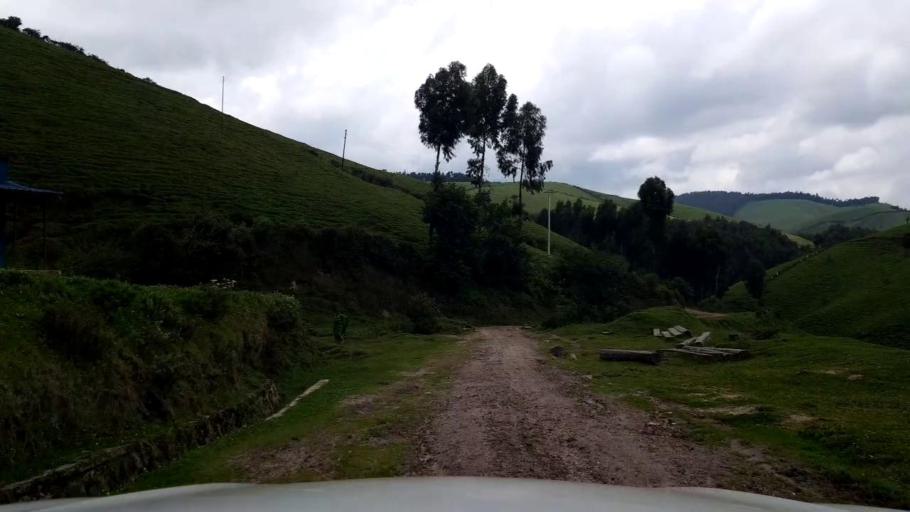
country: RW
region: Western Province
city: Gisenyi
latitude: -1.6830
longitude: 29.4178
